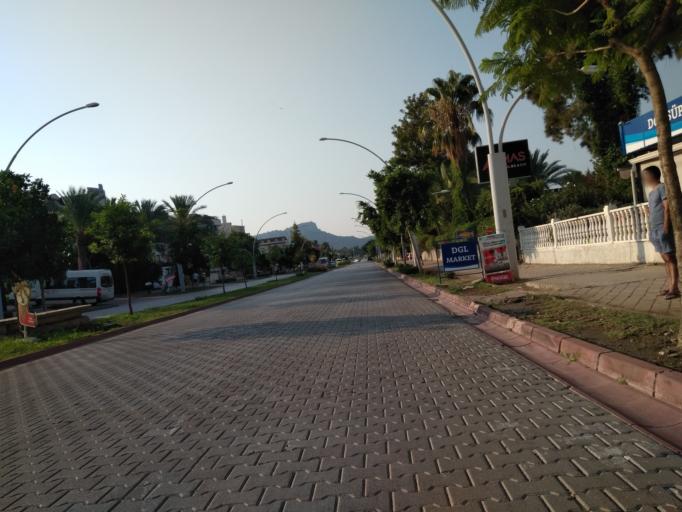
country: TR
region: Antalya
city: Kemer
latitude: 36.6164
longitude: 30.5553
